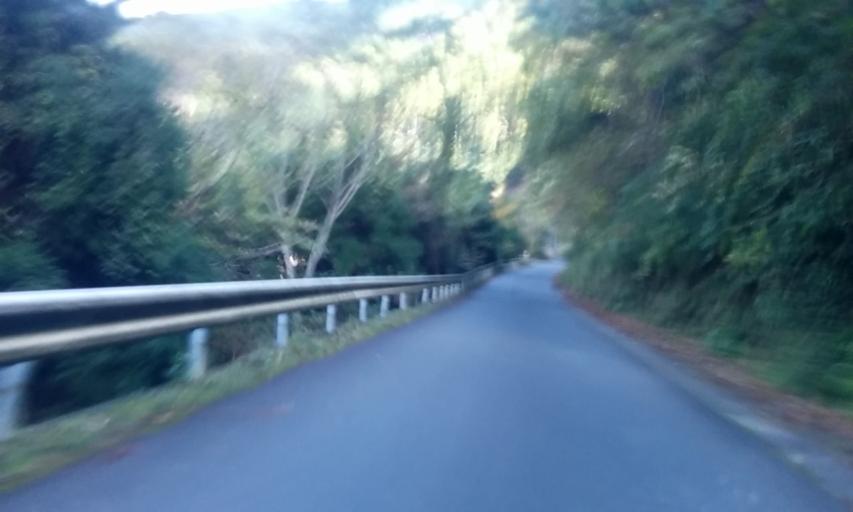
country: JP
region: Kyoto
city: Kameoka
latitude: 35.1366
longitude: 135.5763
